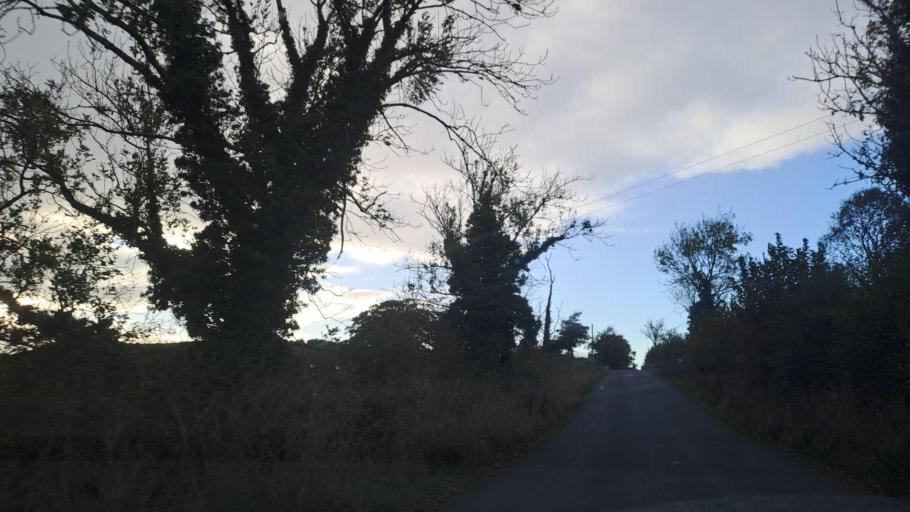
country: IE
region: Ulster
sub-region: County Monaghan
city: Castleblayney
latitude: 54.0433
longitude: -6.8455
